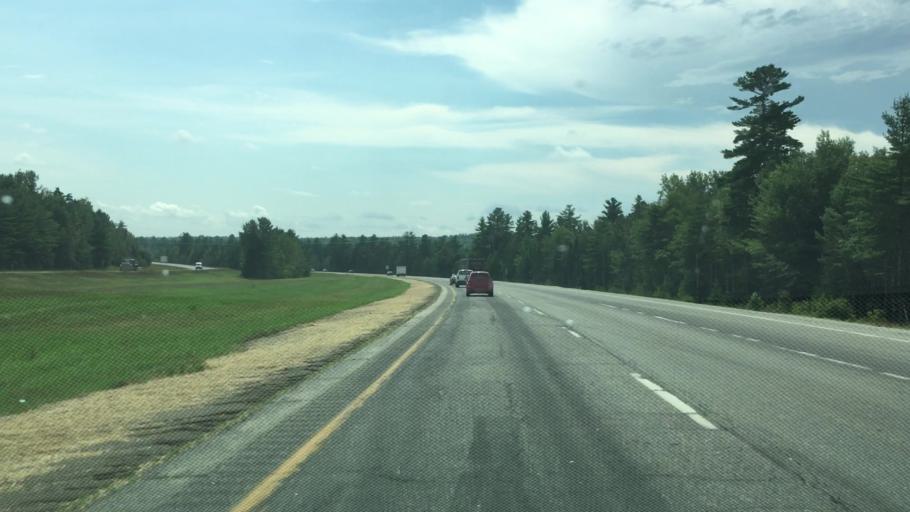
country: US
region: Maine
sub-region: Penobscot County
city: Medway
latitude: 45.5940
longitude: -68.5398
